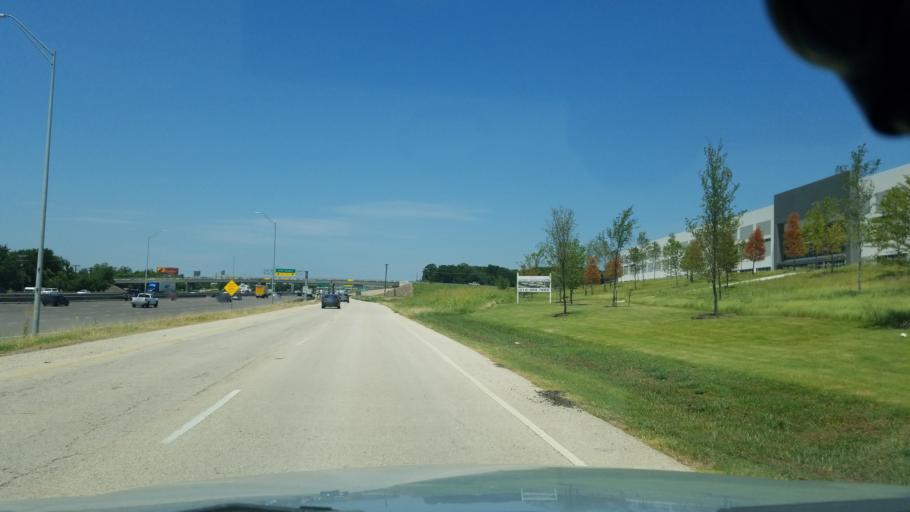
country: US
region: Texas
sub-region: Tarrant County
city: Euless
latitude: 32.8375
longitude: -97.0266
